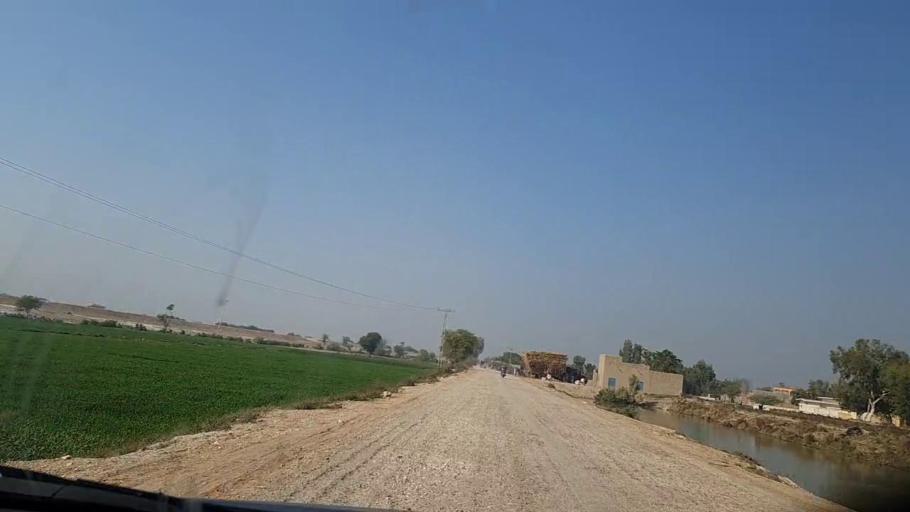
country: PK
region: Sindh
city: Moro
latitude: 26.7381
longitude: 67.9190
